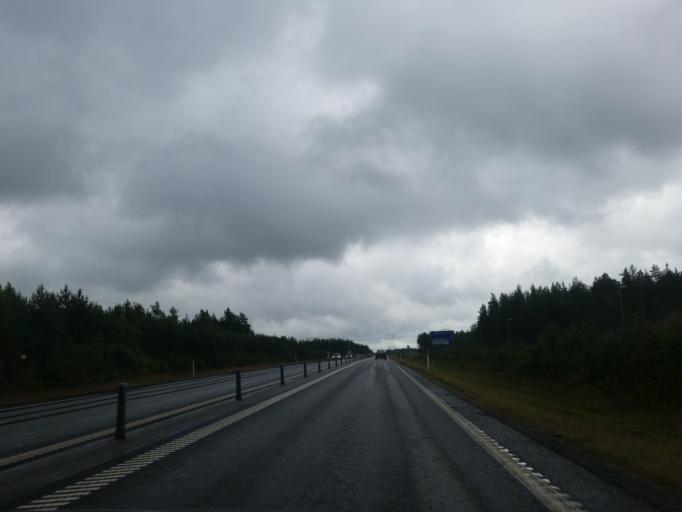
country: SE
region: Vaesterbotten
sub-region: Umea Kommun
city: Taftea
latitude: 63.8590
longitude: 20.4022
